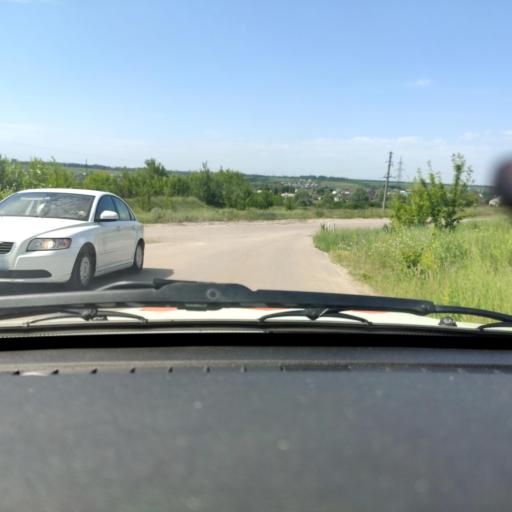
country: RU
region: Voronezj
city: Devitsa
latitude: 51.6255
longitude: 38.9523
